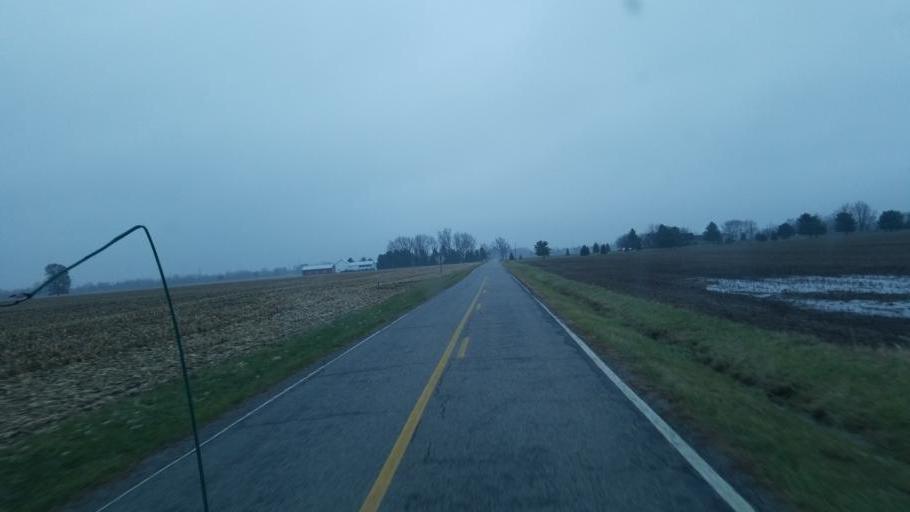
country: US
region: Ohio
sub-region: Delaware County
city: Delaware
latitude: 40.2817
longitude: -82.9996
